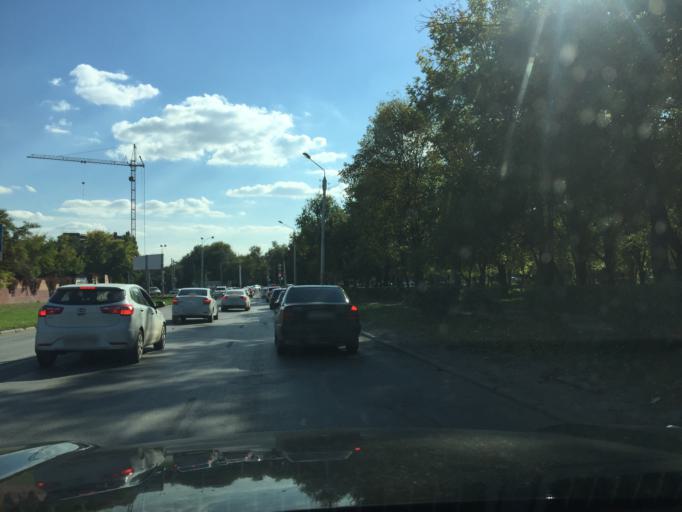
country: RU
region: Rostov
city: Rostov-na-Donu
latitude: 47.2137
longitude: 39.6463
